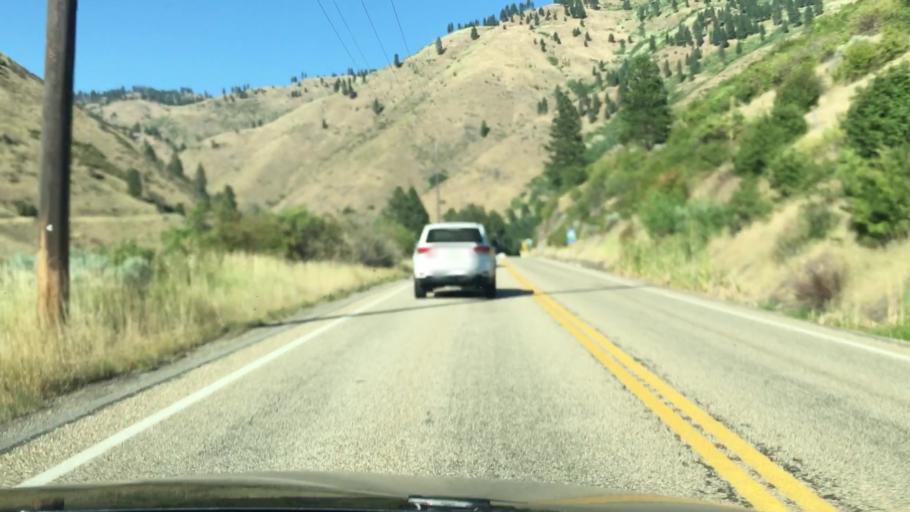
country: US
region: Idaho
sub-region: Boise County
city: Idaho City
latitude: 44.0241
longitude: -116.1448
